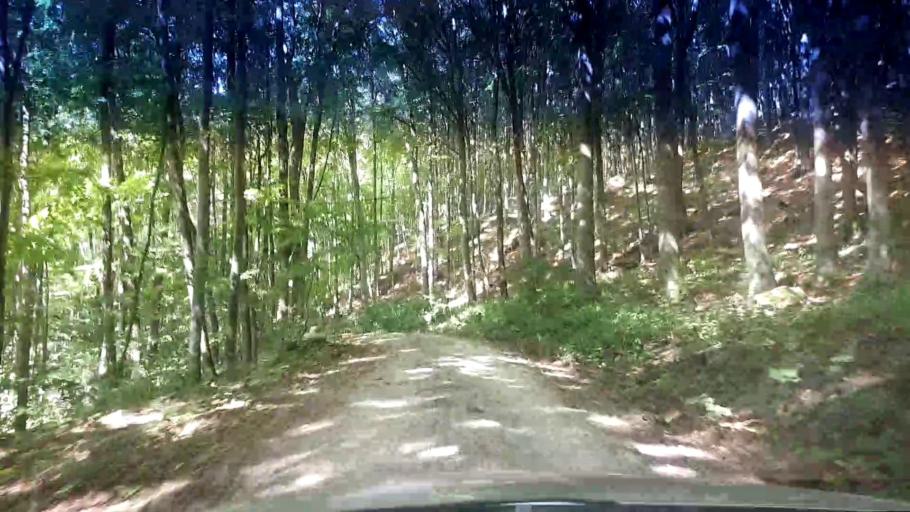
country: DE
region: Bavaria
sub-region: Upper Franconia
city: Schesslitz
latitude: 49.9455
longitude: 11.0685
